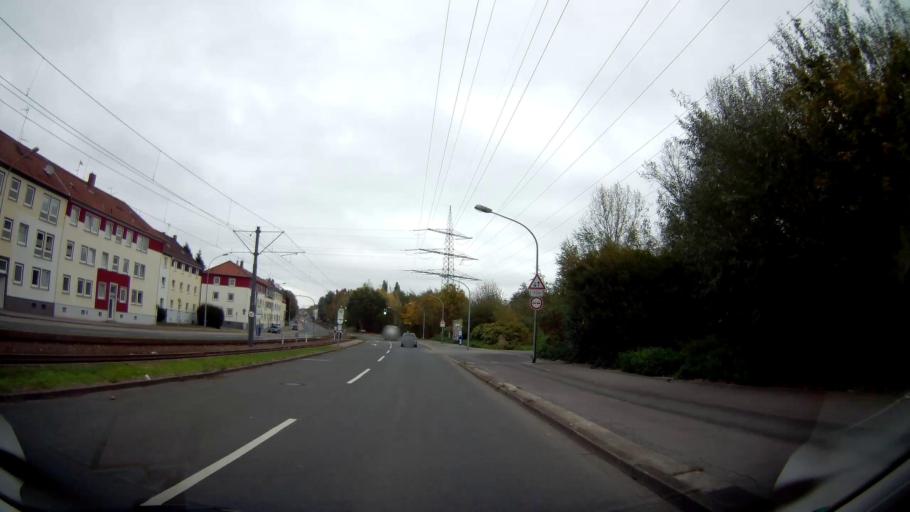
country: DE
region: North Rhine-Westphalia
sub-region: Regierungsbezirk Munster
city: Gladbeck
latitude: 51.5439
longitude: 7.0364
